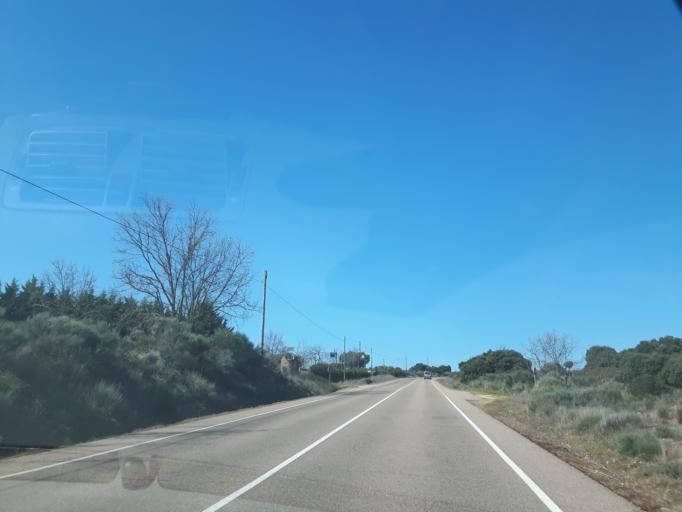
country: ES
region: Castille and Leon
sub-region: Provincia de Salamanca
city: Bermellar
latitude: 40.9586
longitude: -6.6524
